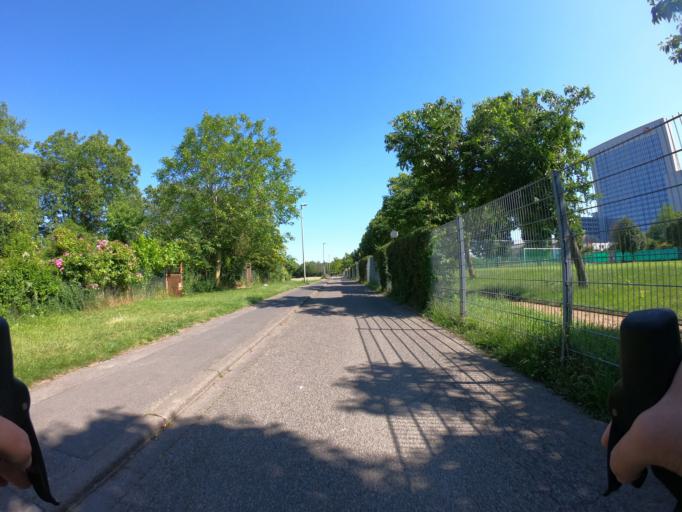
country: DE
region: Hesse
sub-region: Regierungsbezirk Darmstadt
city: Eschborn
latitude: 50.1355
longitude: 8.5771
